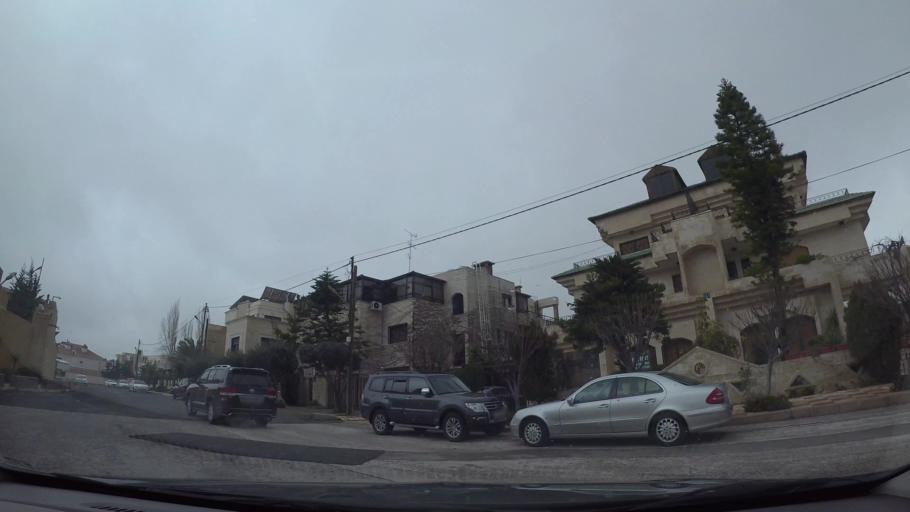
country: JO
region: Amman
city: Al Bunayyat ash Shamaliyah
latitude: 31.9456
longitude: 35.8829
